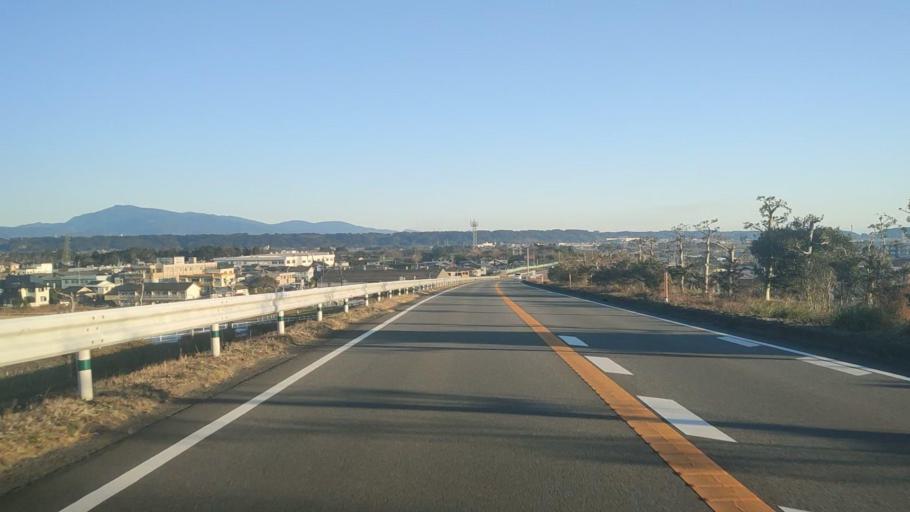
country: JP
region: Miyazaki
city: Tsuma
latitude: 32.0335
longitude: 131.4652
